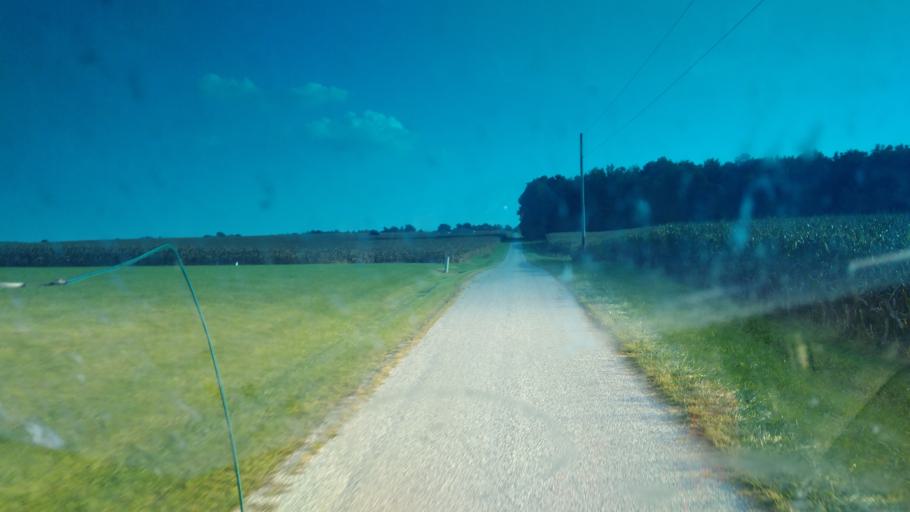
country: US
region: Ohio
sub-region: Crawford County
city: Bucyrus
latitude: 40.9175
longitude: -82.9975
